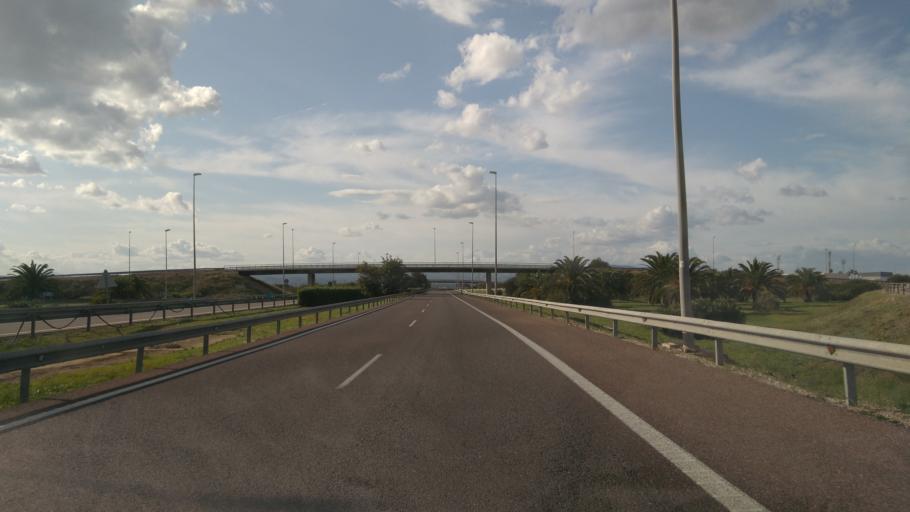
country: ES
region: Valencia
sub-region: Provincia de Valencia
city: Guadassuar
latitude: 39.1769
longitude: -0.4738
